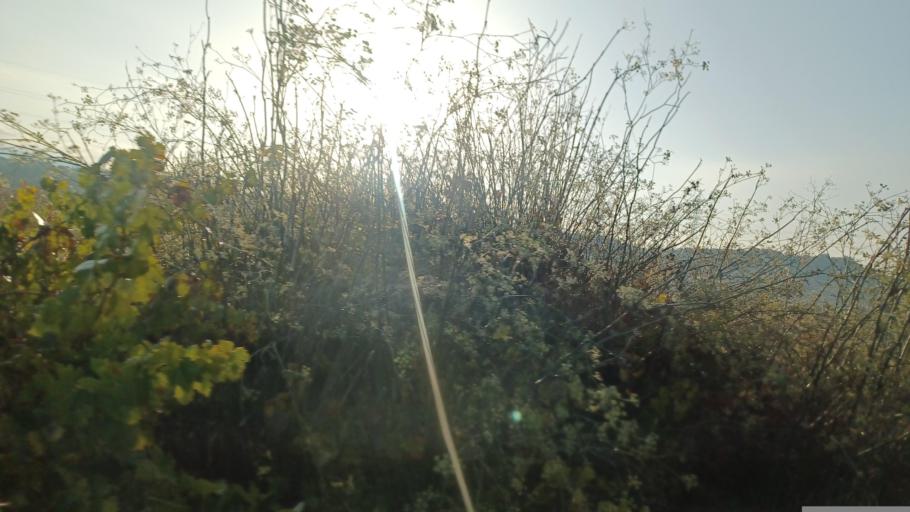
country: CY
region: Pafos
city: Tala
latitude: 34.8879
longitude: 32.4903
